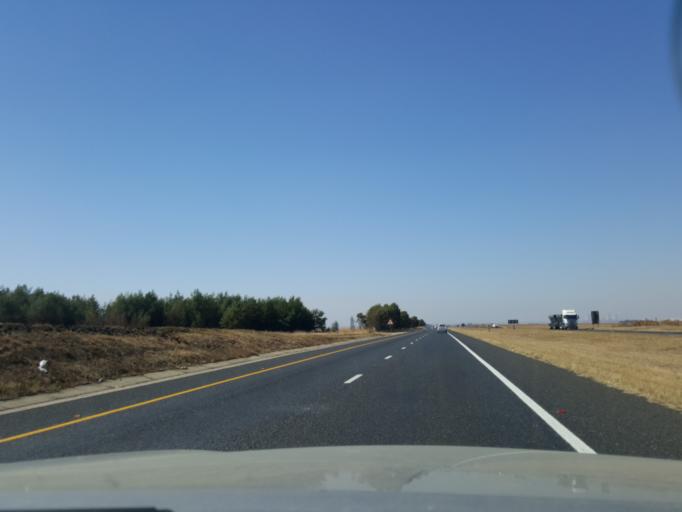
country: ZA
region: Mpumalanga
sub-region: Nkangala District Municipality
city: Delmas
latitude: -26.0701
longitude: 28.7579
